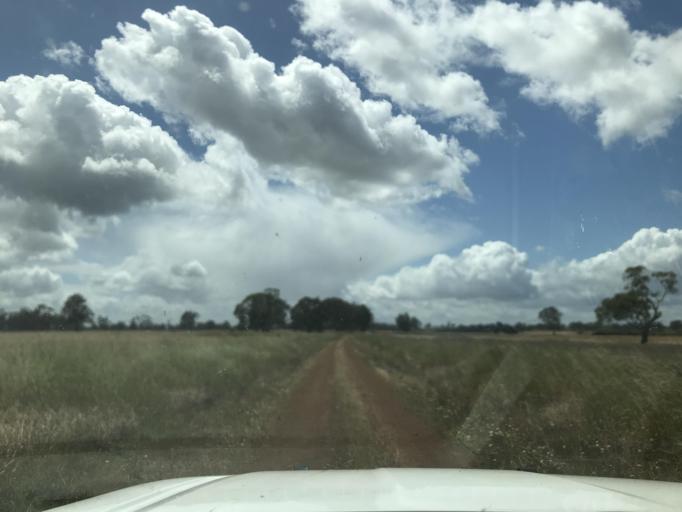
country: AU
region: South Australia
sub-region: Wattle Range
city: Penola
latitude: -37.1838
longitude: 141.4672
